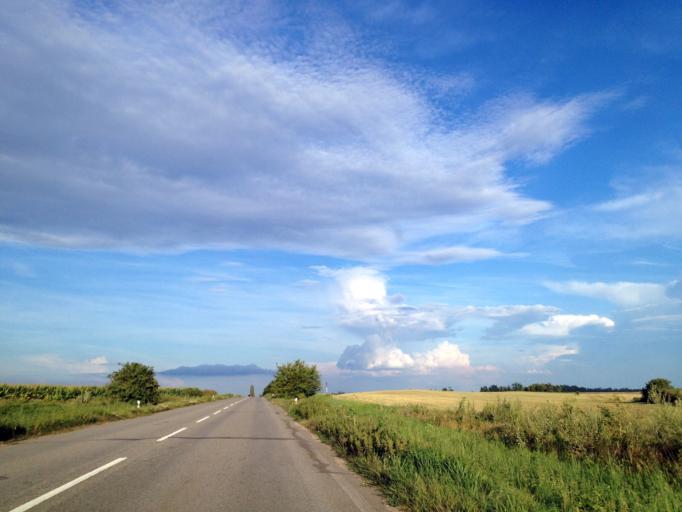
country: SK
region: Nitriansky
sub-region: Okres Komarno
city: Hurbanovo
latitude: 47.9060
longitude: 18.3345
